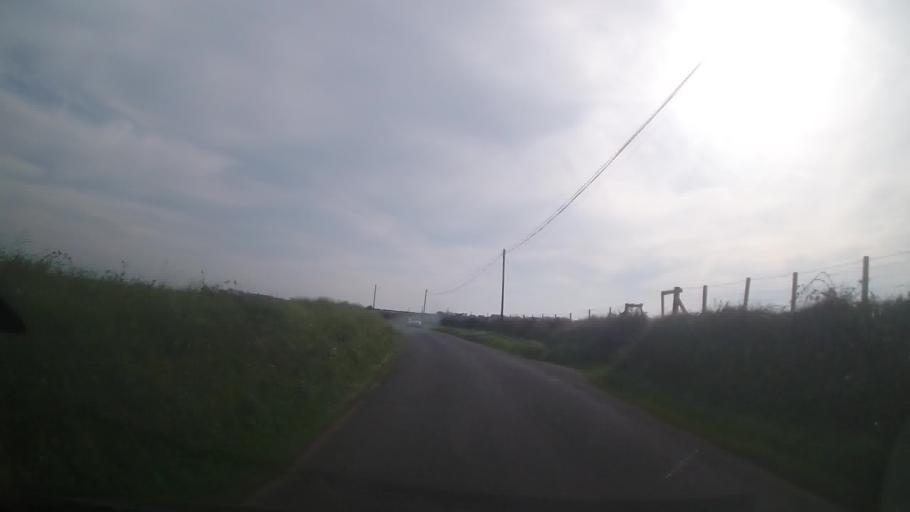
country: GB
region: Wales
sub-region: Pembrokeshire
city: Saint David's
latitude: 51.8961
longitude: -5.2483
